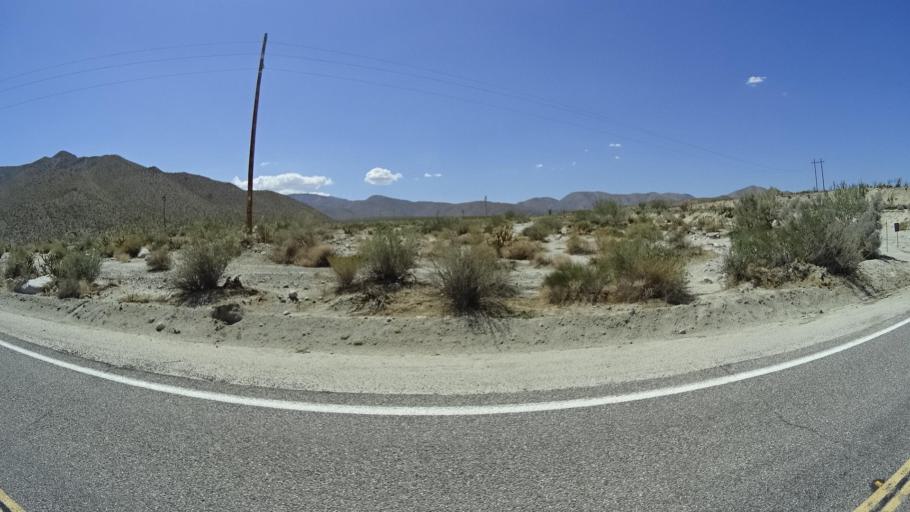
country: US
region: California
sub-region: San Diego County
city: Borrego Springs
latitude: 33.1324
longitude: -116.3121
